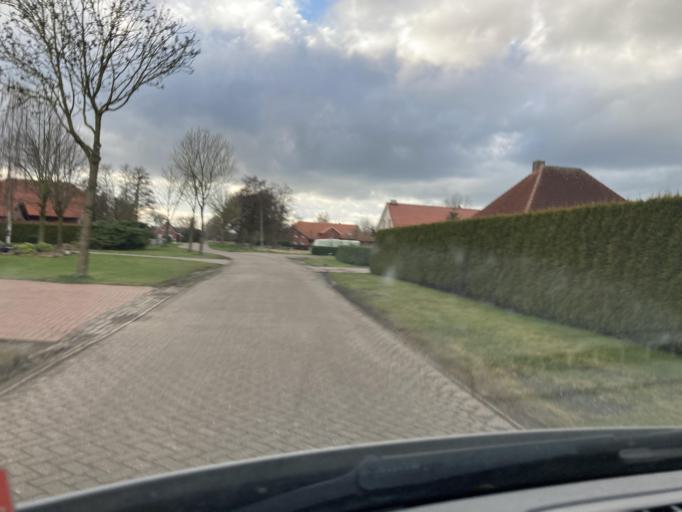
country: DE
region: Lower Saxony
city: Ostrhauderfehn
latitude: 53.1383
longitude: 7.5530
